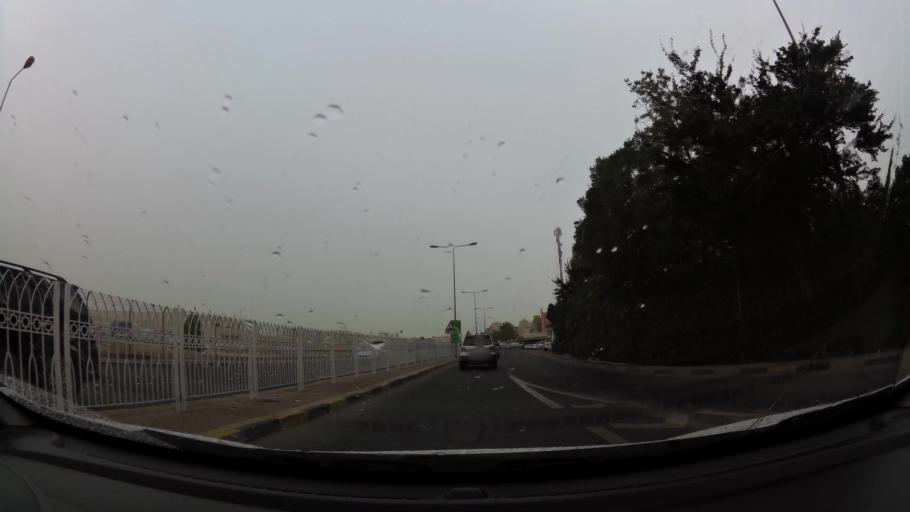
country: BH
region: Northern
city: Madinat `Isa
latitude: 26.1706
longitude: 50.5571
